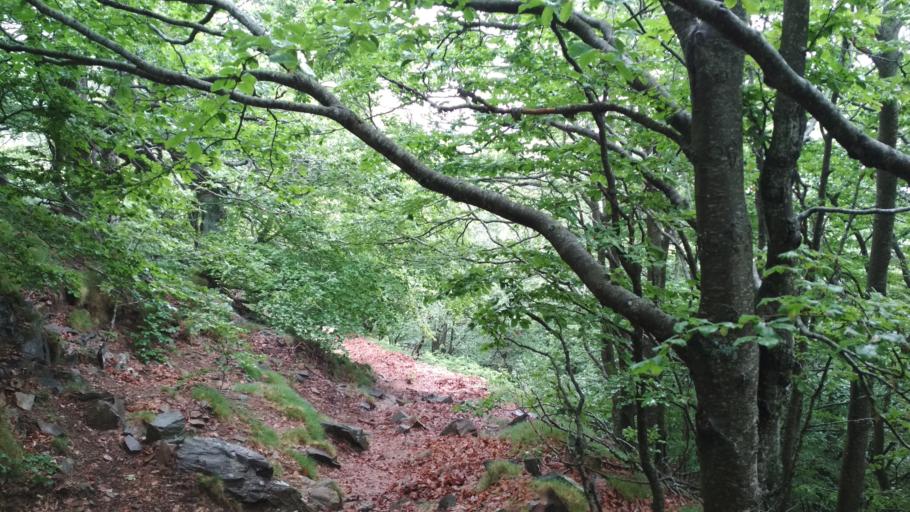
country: ES
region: Catalonia
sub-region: Provincia de Barcelona
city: Fogars de Montclus
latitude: 41.7809
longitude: 2.4350
